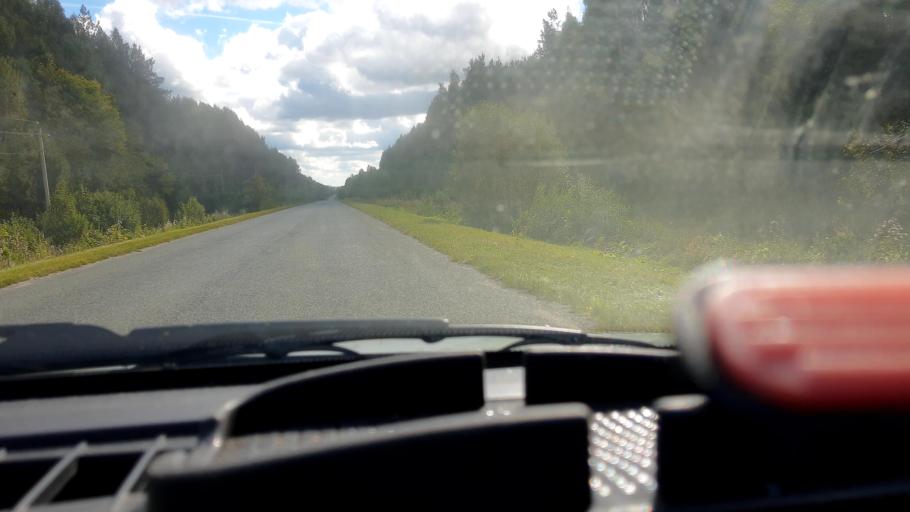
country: RU
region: Mariy-El
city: Kilemary
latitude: 56.9218
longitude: 46.7142
